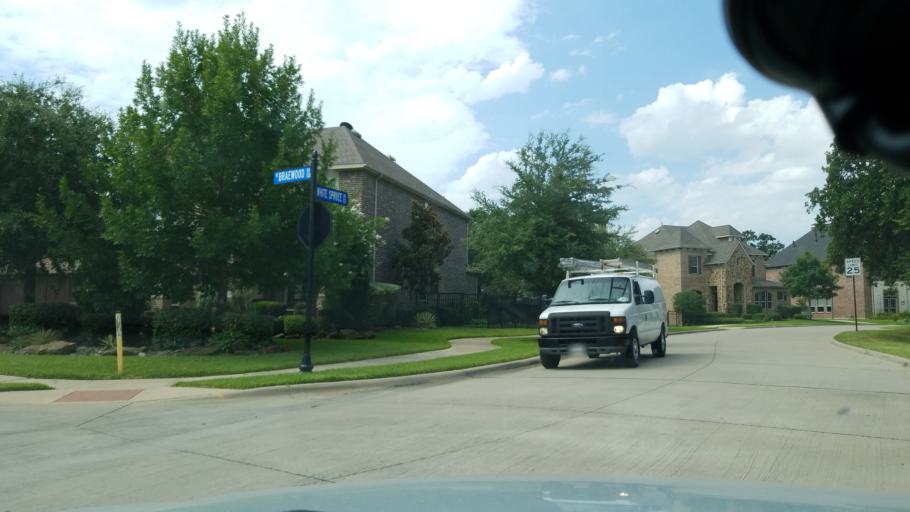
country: US
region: Texas
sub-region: Dallas County
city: Coppell
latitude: 32.9666
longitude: -96.9958
